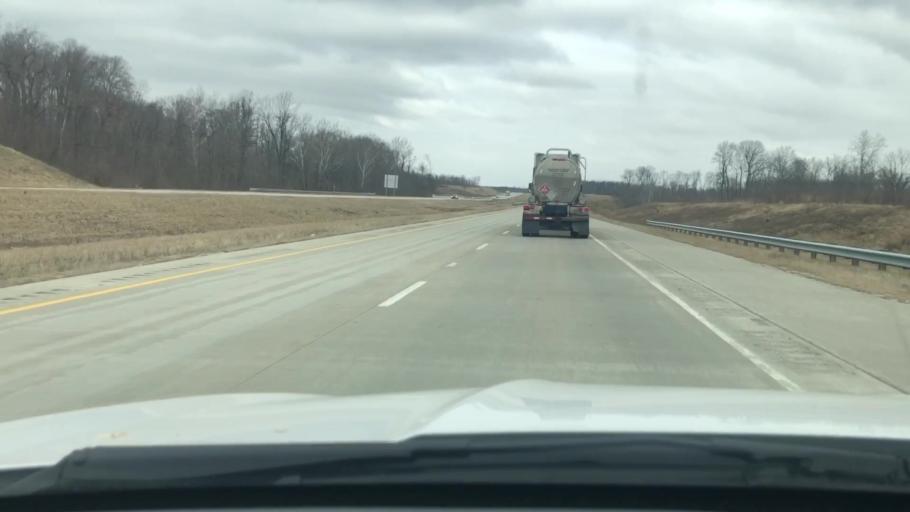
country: US
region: Indiana
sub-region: Carroll County
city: Delphi
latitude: 40.5773
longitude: -86.6474
